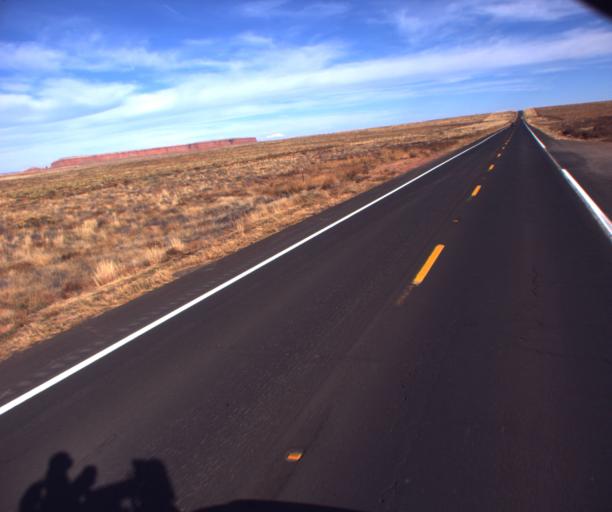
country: US
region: Arizona
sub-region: Apache County
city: Lukachukai
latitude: 36.9621
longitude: -109.4211
